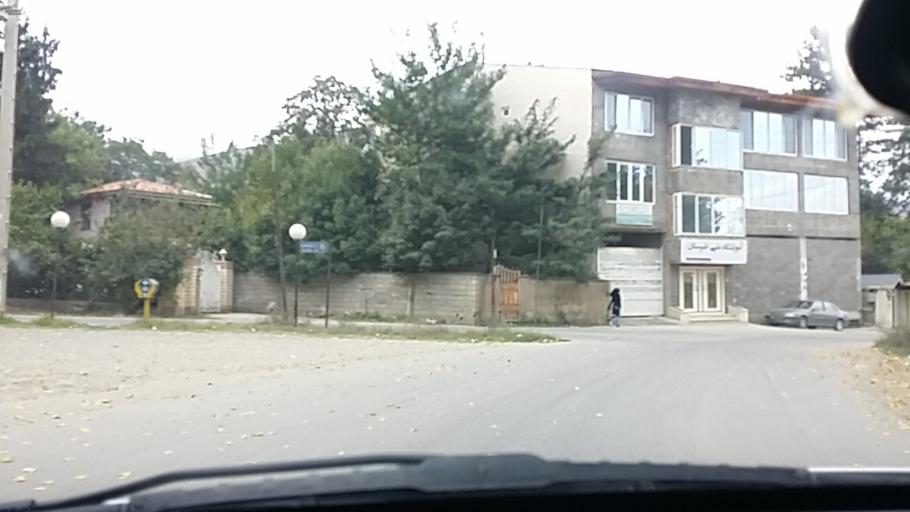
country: IR
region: Mazandaran
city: `Abbasabad
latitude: 36.5035
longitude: 51.1614
